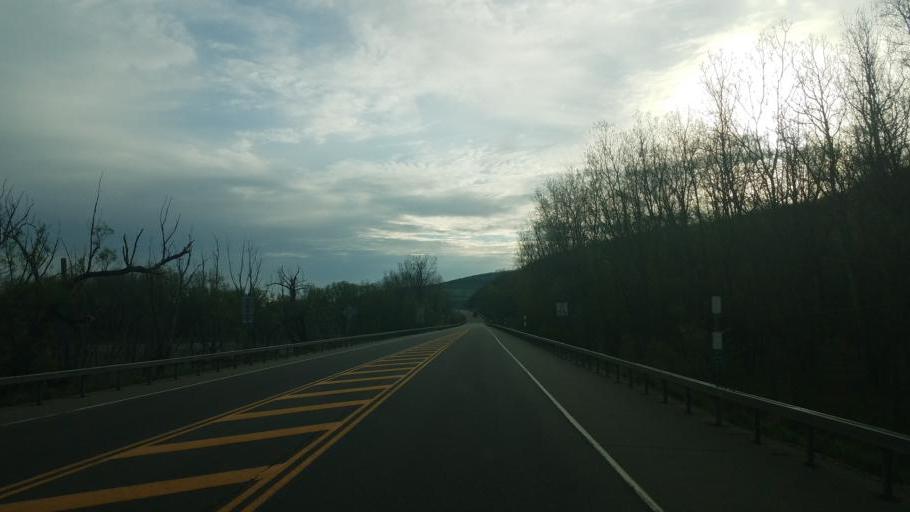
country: US
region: New York
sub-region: Steuben County
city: Hornell
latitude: 42.3388
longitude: -77.7212
